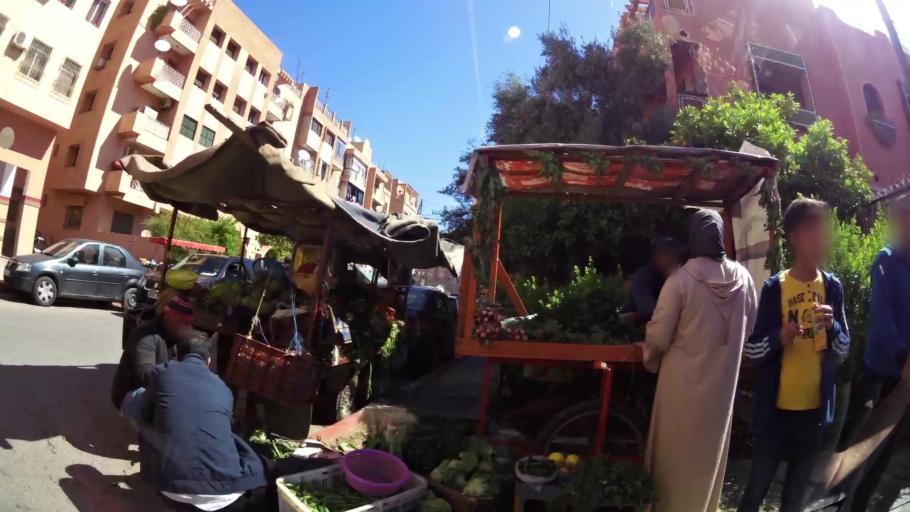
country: MA
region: Marrakech-Tensift-Al Haouz
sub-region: Marrakech
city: Marrakesh
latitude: 31.6448
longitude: -8.0108
